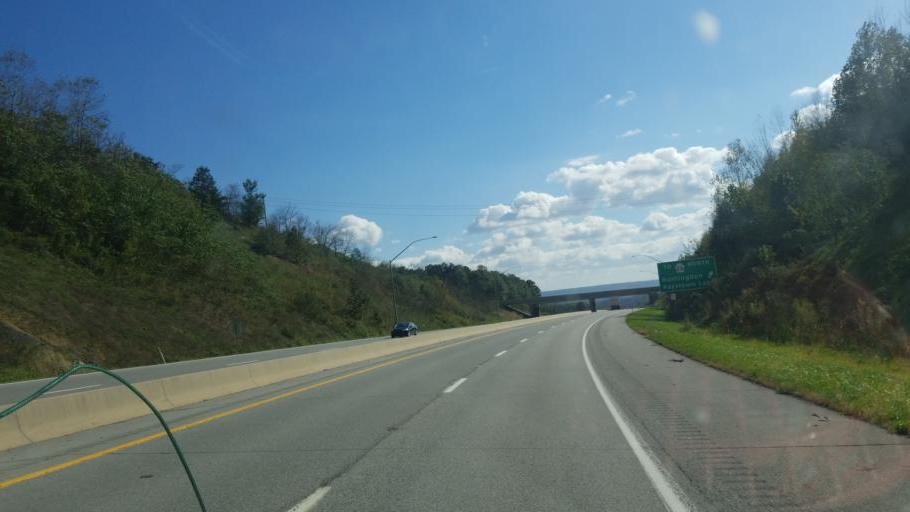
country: US
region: Pennsylvania
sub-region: Bedford County
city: Everett
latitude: 40.0273
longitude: -78.3706
